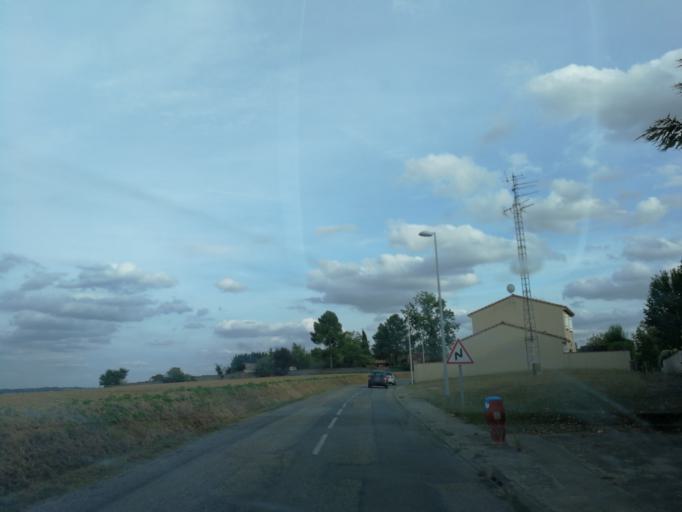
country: FR
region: Midi-Pyrenees
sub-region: Departement de la Haute-Garonne
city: Flourens
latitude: 43.5941
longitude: 1.5719
